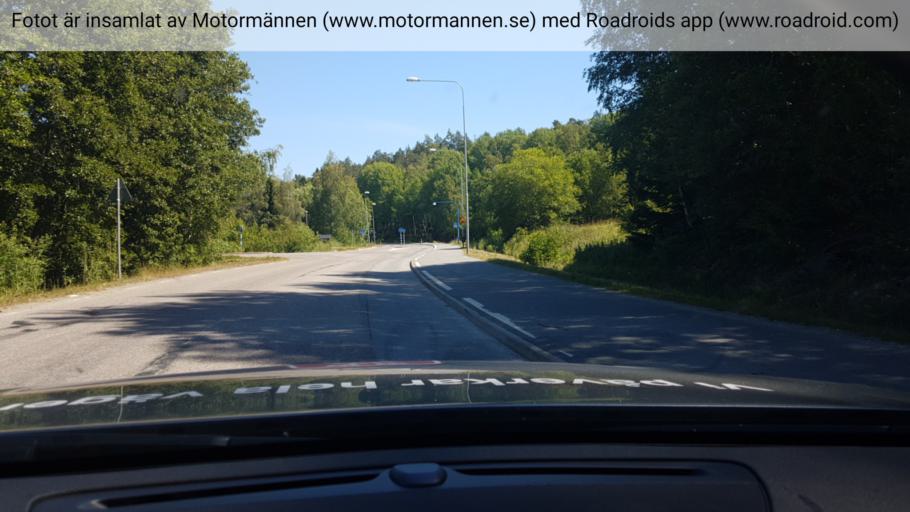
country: SE
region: Stockholm
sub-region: Haninge Kommun
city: Haninge
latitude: 59.1875
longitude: 18.1575
